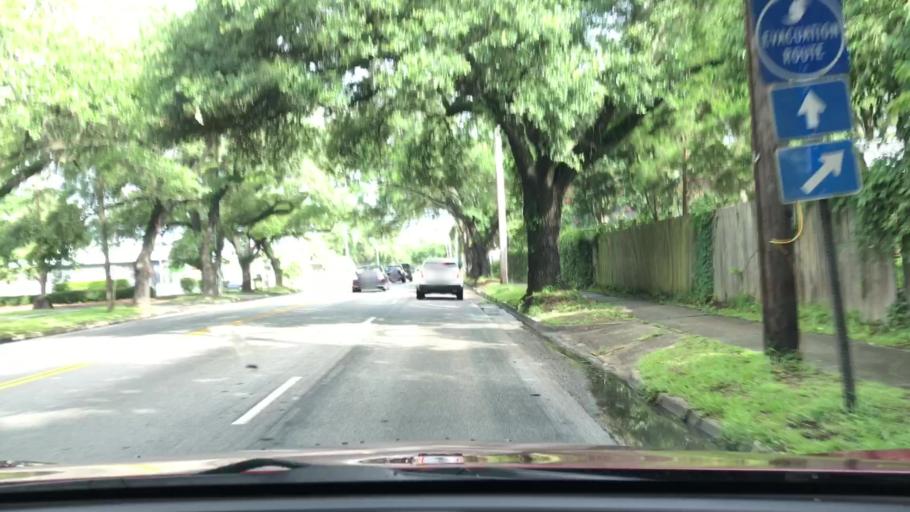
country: US
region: South Carolina
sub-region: Georgetown County
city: Georgetown
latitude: 33.3729
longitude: -79.2820
